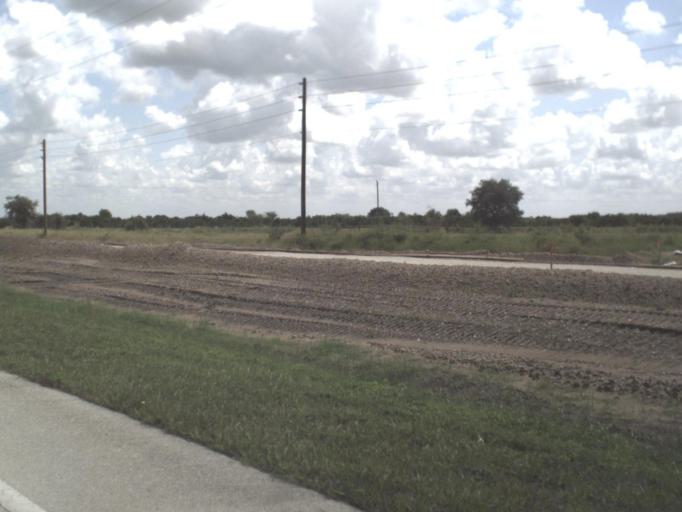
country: US
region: Florida
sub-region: DeSoto County
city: Nocatee
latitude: 27.0954
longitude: -81.9435
